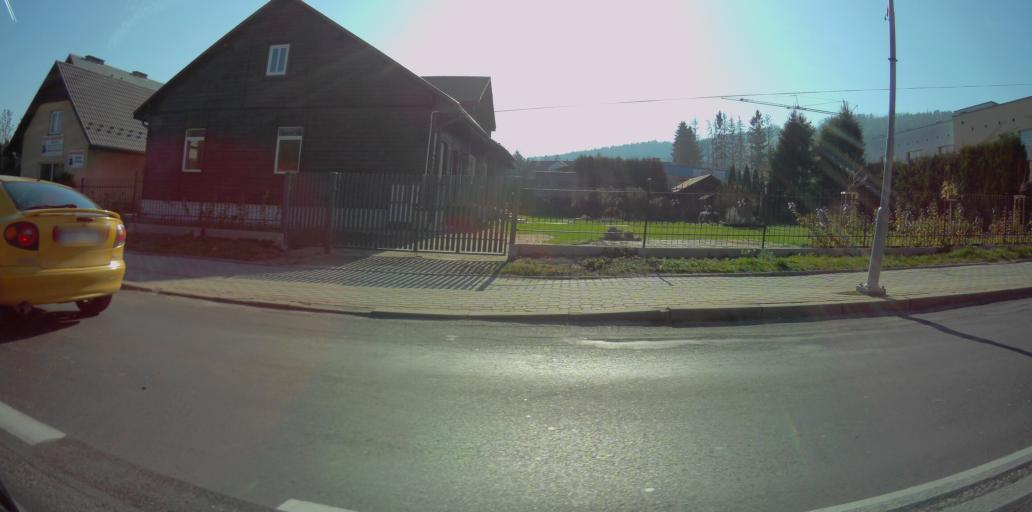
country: PL
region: Subcarpathian Voivodeship
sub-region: Powiat bieszczadzki
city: Ustrzyki Dolne
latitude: 49.4309
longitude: 22.5980
